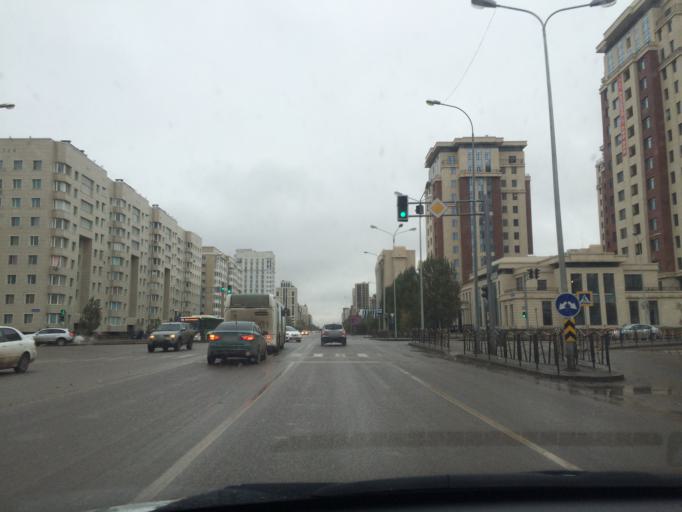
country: KZ
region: Astana Qalasy
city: Astana
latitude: 51.1153
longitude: 71.4169
